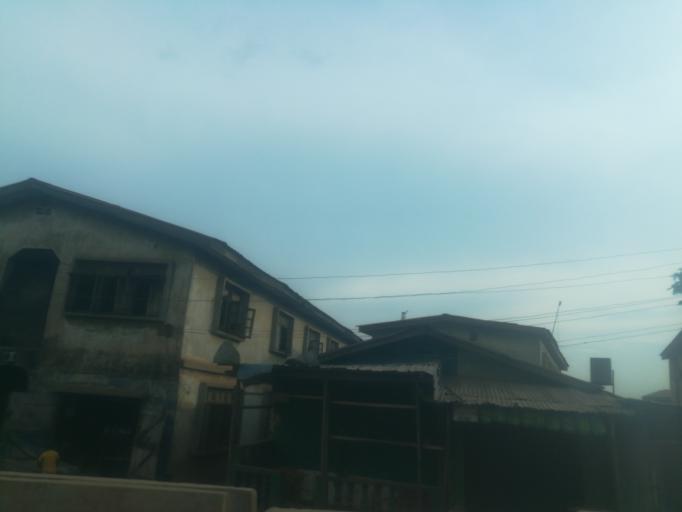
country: NG
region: Ogun
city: Abeokuta
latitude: 7.1581
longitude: 3.3243
